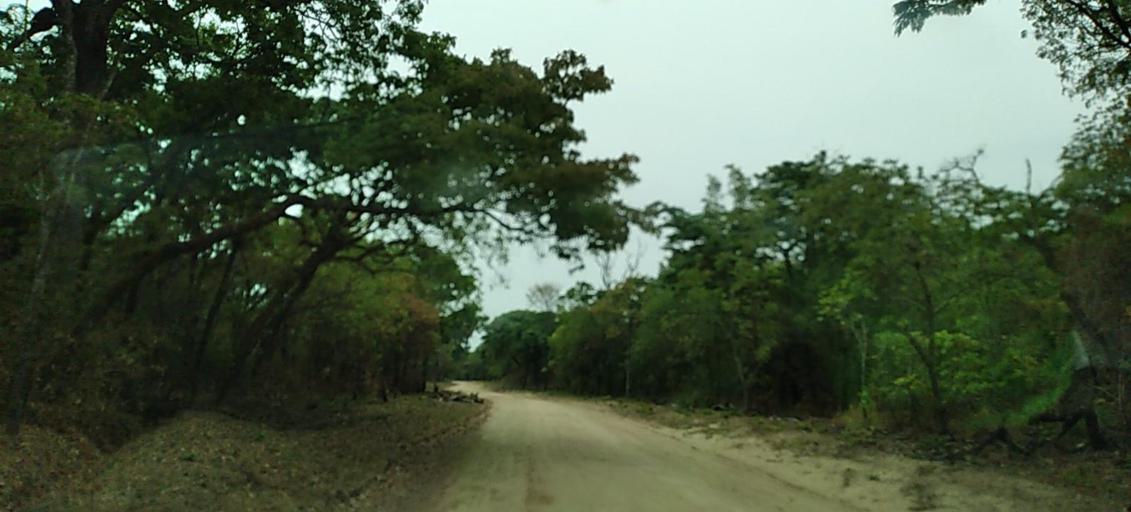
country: ZM
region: North-Western
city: Solwezi
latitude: -12.5350
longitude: 26.5231
